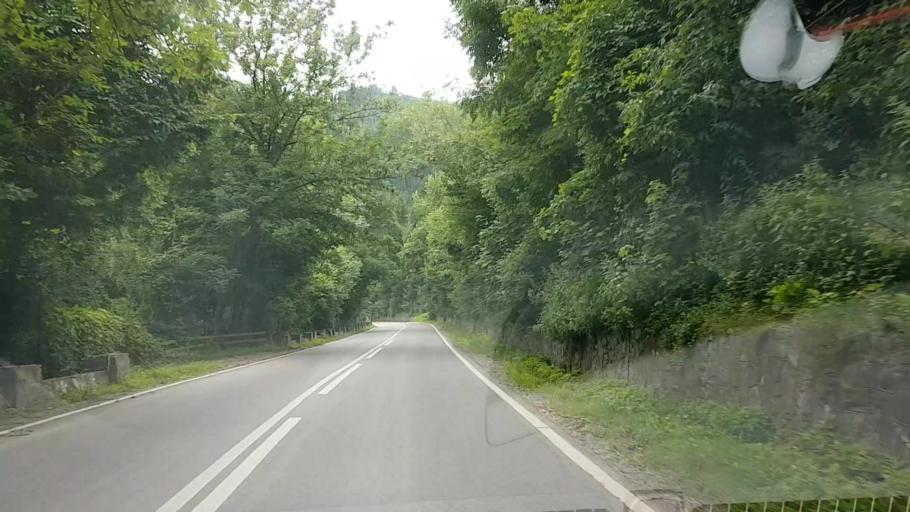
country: RO
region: Neamt
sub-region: Comuna Poiana Teiului
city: Poiana Teiului
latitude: 47.0987
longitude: 25.9416
